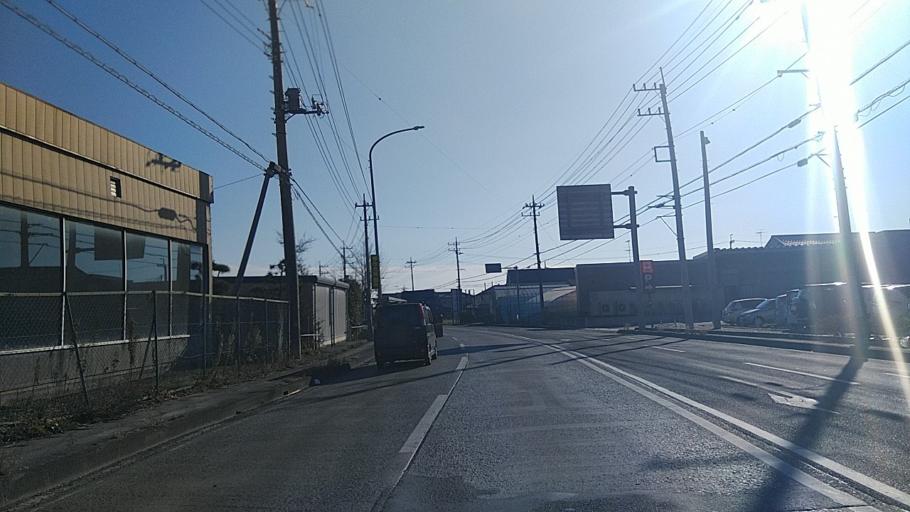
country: JP
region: Tochigi
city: Tanuma
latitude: 36.3671
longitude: 139.5743
